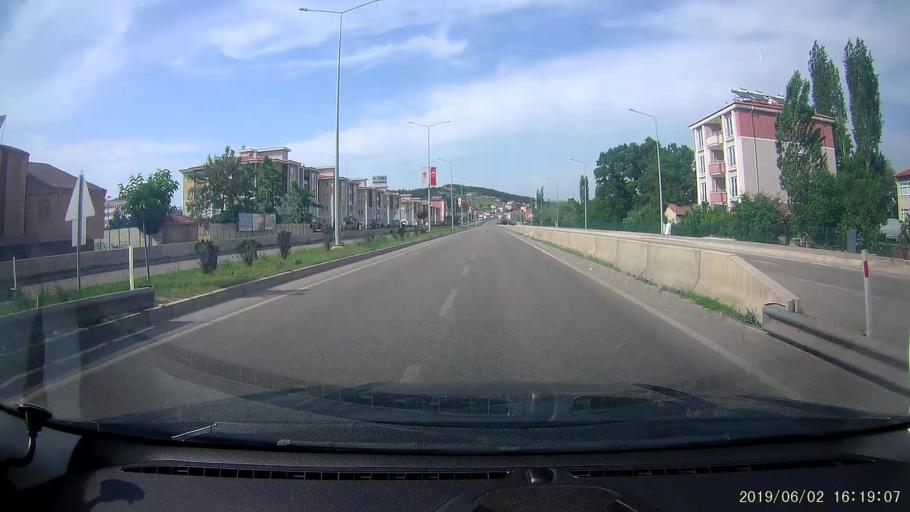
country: TR
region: Samsun
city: Havza
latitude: 40.9634
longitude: 35.6671
